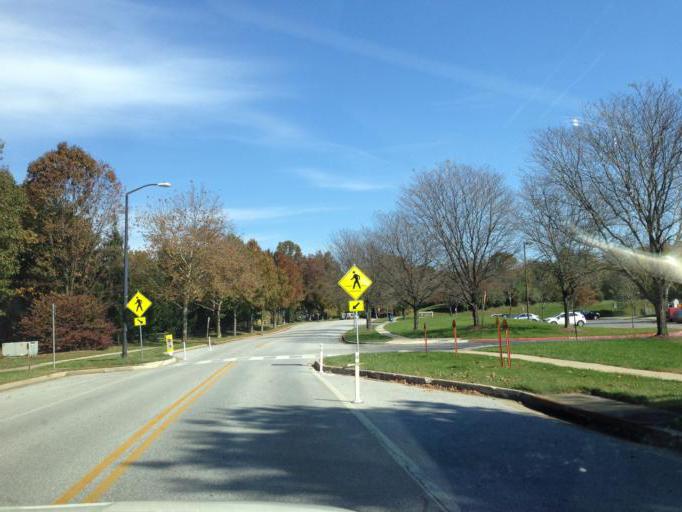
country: US
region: Maryland
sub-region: Howard County
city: Columbia
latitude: 39.2499
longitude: -76.8403
